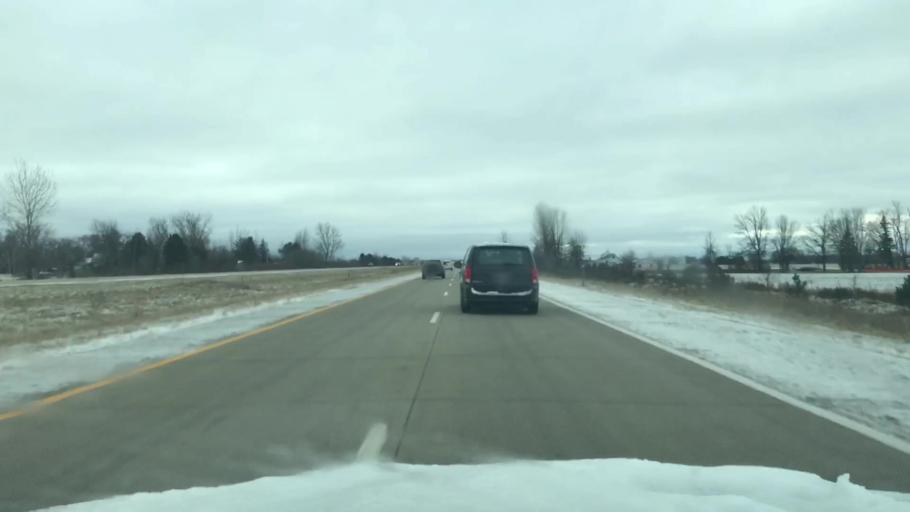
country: US
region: Michigan
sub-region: Bay County
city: Pinconning
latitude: 43.8218
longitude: -84.0207
